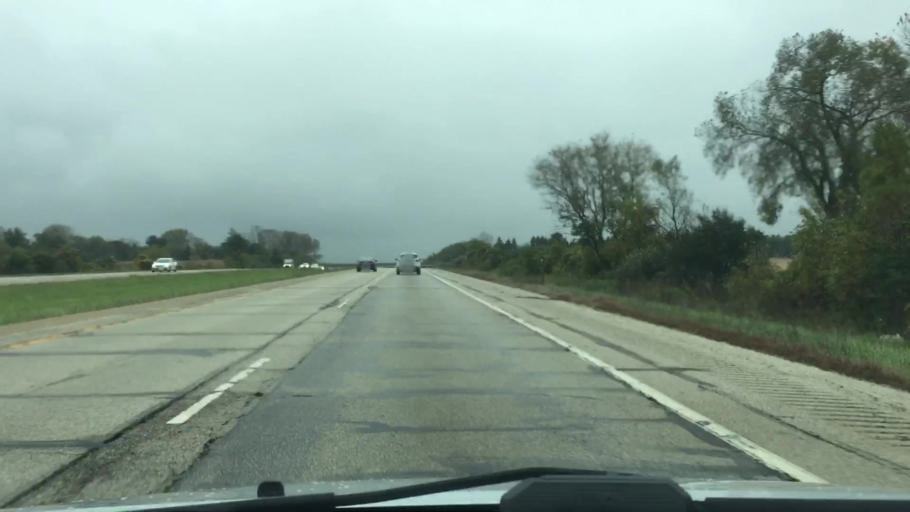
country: US
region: Wisconsin
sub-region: Walworth County
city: Como
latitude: 42.6321
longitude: -88.4744
